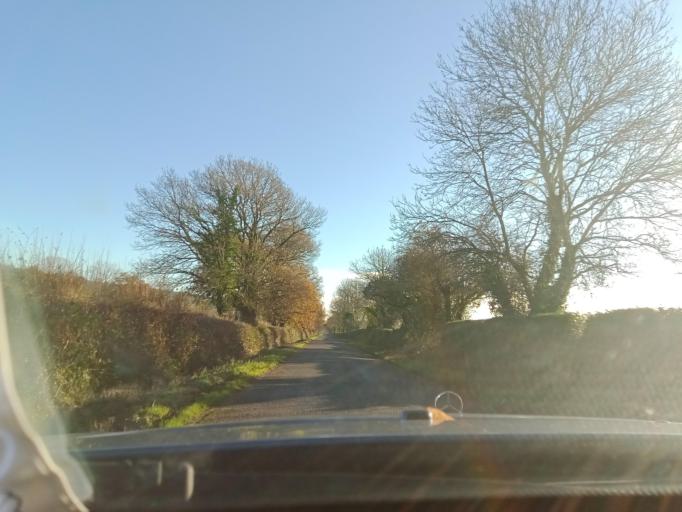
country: IE
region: Leinster
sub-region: Kilkenny
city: Piltown
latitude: 52.3586
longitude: -7.3054
